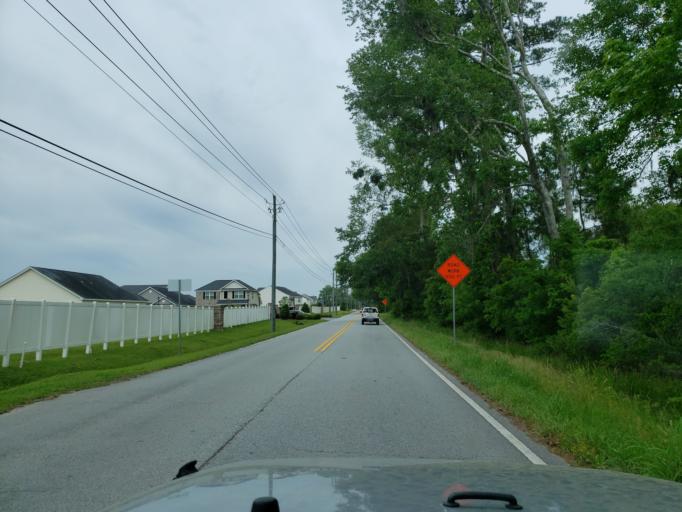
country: US
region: Georgia
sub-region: Chatham County
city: Port Wentworth
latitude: 32.1846
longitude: -81.2173
